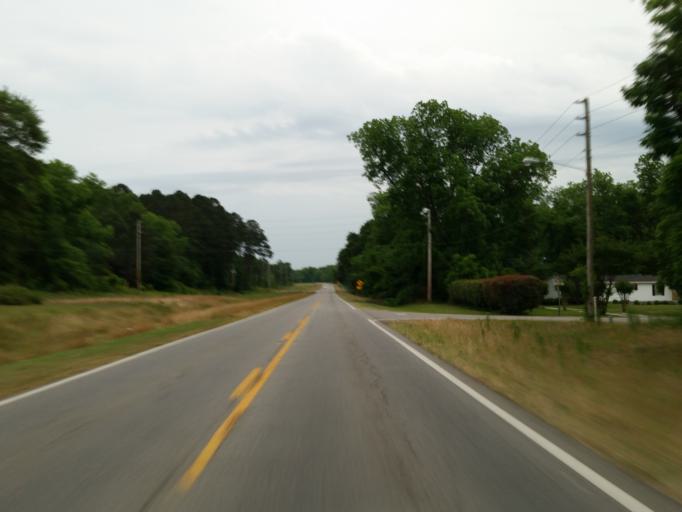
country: US
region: Georgia
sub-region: Crisp County
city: Cordele
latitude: 32.0076
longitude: -83.7934
